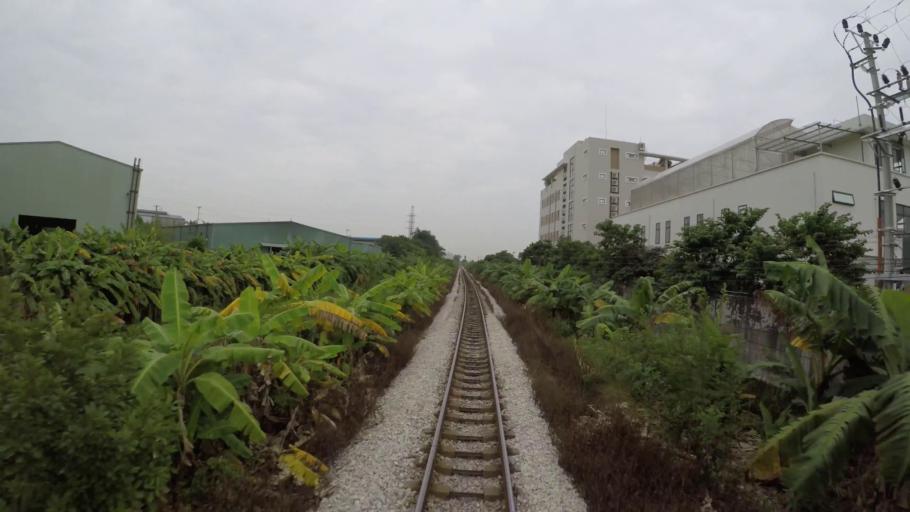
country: VN
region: Hai Phong
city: An Duong
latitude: 20.8988
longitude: 106.5806
